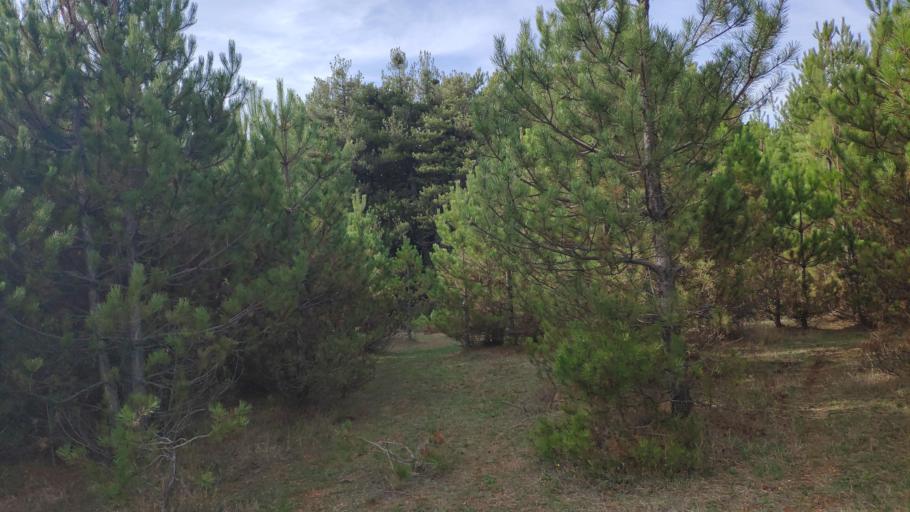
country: GR
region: West Greece
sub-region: Nomos Achaias
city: Aiyira
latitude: 38.0339
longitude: 22.3741
